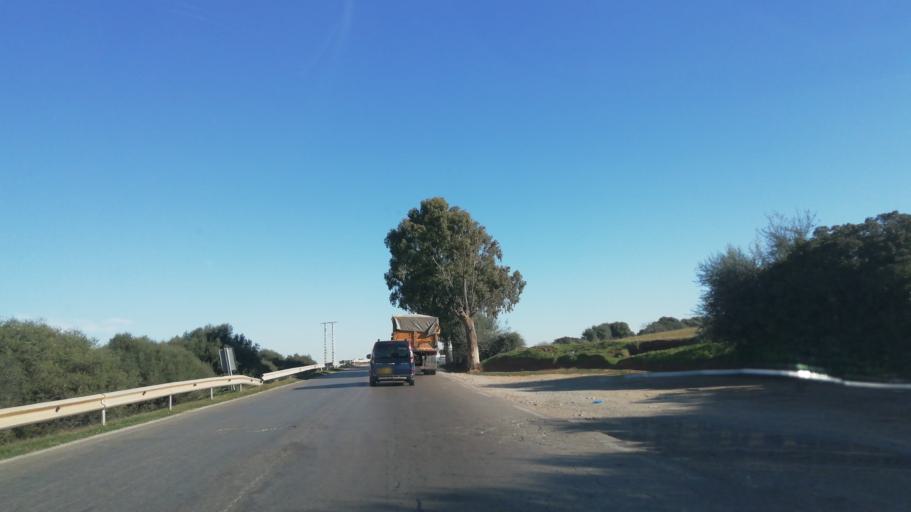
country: DZ
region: Relizane
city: Smala
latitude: 35.6967
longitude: 0.7800
